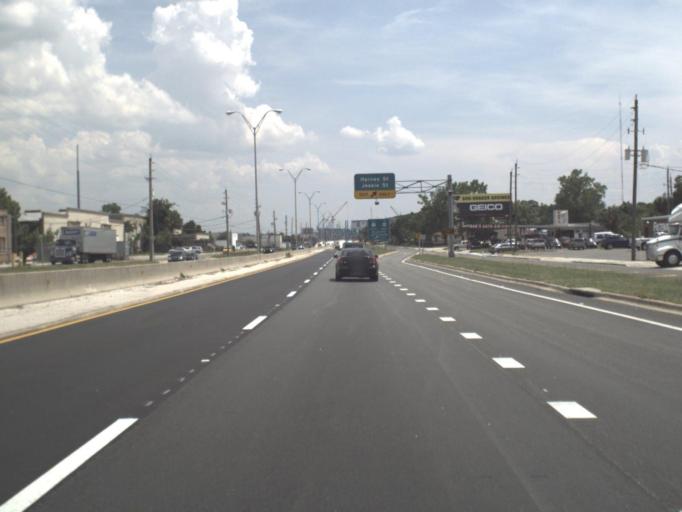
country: US
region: Florida
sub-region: Duval County
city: Jacksonville
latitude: 30.3416
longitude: -81.6368
